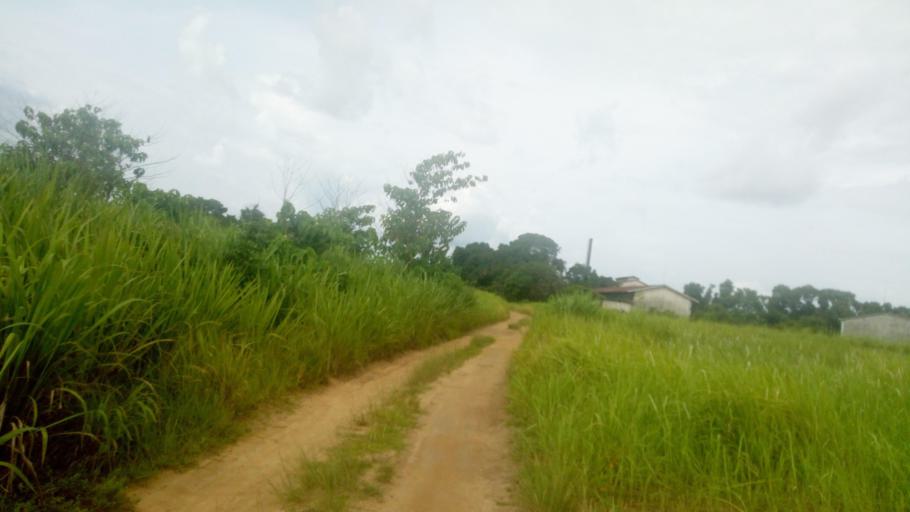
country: SL
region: Northern Province
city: Magburaka
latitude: 8.6732
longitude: -12.0204
